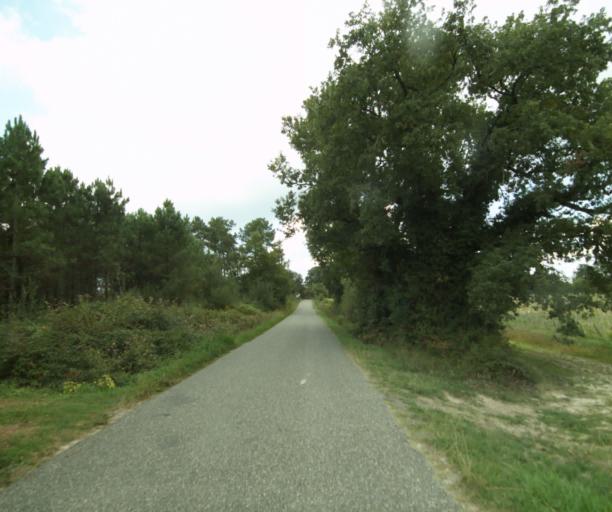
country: FR
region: Midi-Pyrenees
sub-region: Departement du Gers
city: Cazaubon
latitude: 43.8831
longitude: -0.0743
